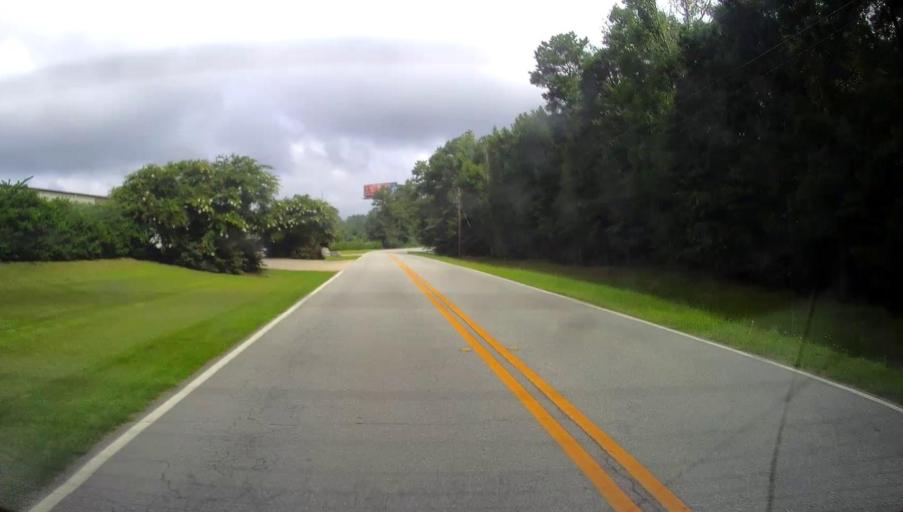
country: US
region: Georgia
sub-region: Bibb County
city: West Point
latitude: 32.8209
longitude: -83.7282
